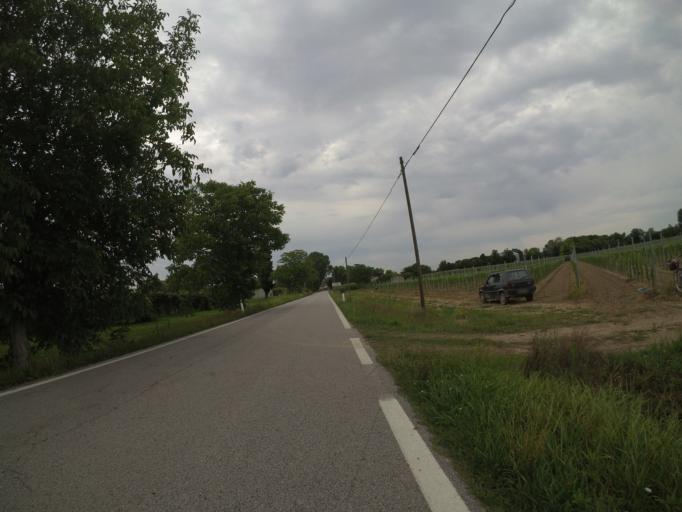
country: IT
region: Friuli Venezia Giulia
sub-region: Provincia di Udine
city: Camino al Tagliamento
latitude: 45.8999
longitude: 12.9463
